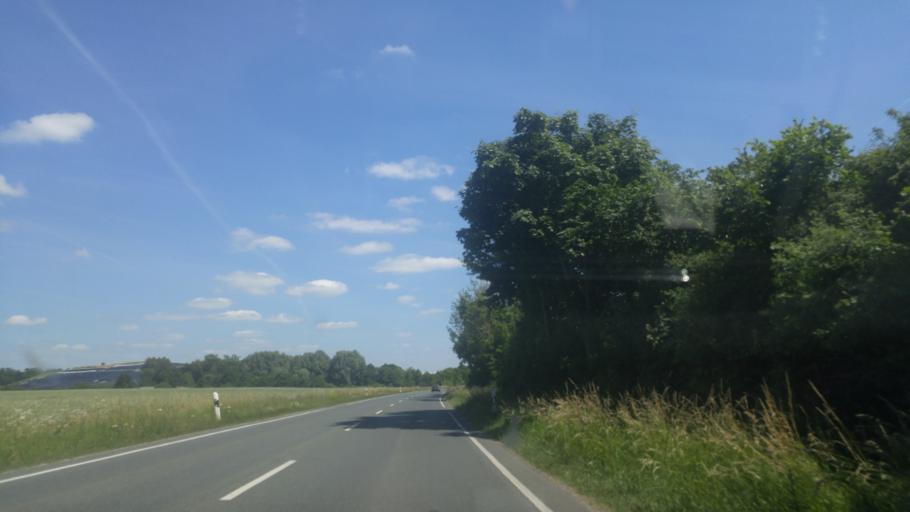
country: DE
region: Bavaria
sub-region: Regierungsbezirk Mittelfranken
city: Herzogenaurach
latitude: 49.5793
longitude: 10.8892
